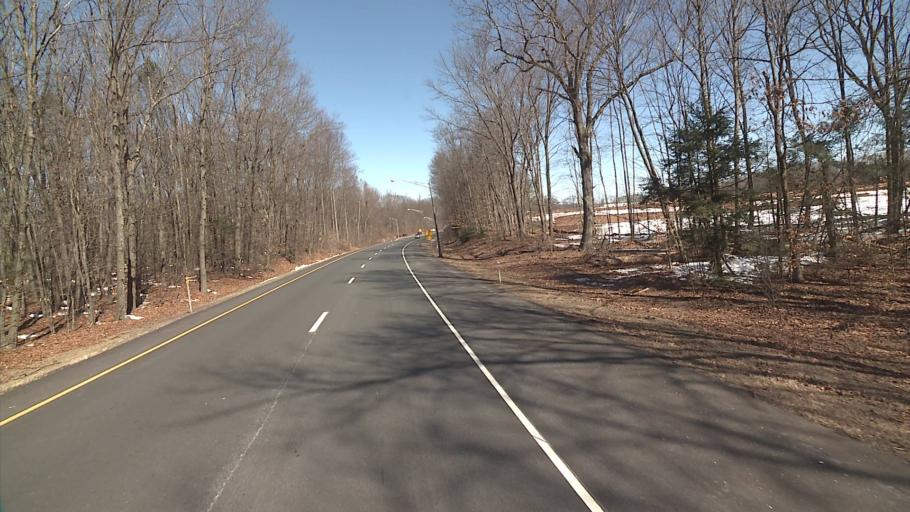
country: US
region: Connecticut
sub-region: Middlesex County
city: Cromwell
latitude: 41.6264
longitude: -72.6867
